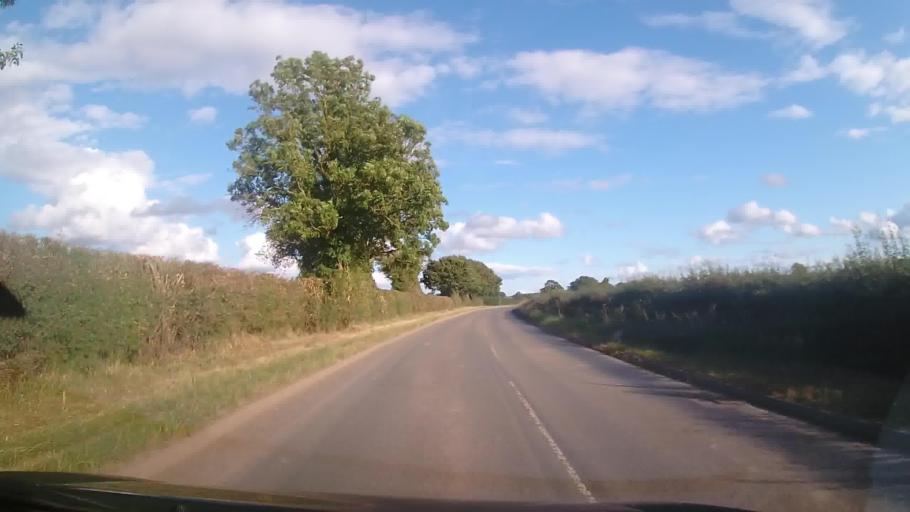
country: GB
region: England
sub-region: Shropshire
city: Great Hanwood
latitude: 52.6586
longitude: -2.8122
